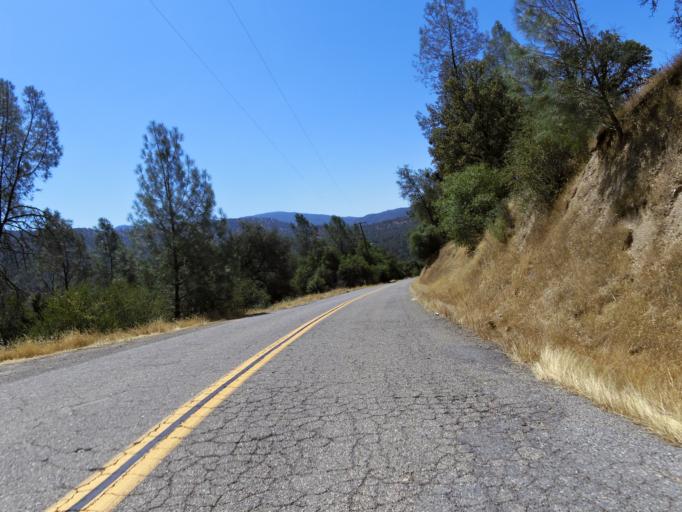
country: US
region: California
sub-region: Fresno County
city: Auberry
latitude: 37.1582
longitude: -119.5139
